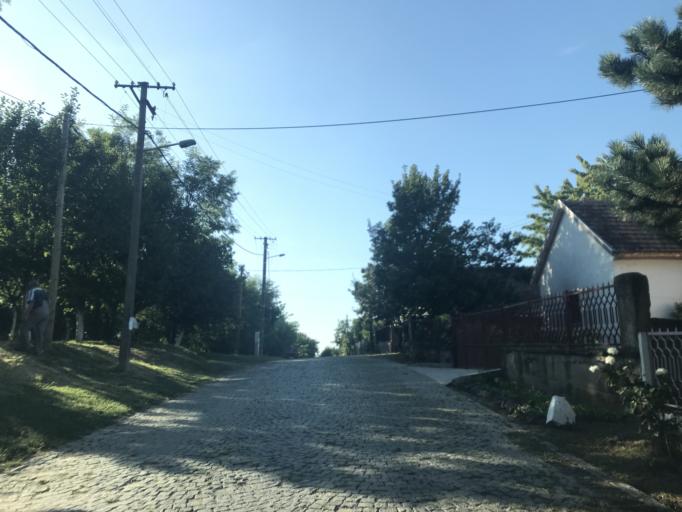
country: RS
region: Autonomna Pokrajina Vojvodina
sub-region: Juznobacki Okrug
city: Novi Sad
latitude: 45.2080
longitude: 19.8011
